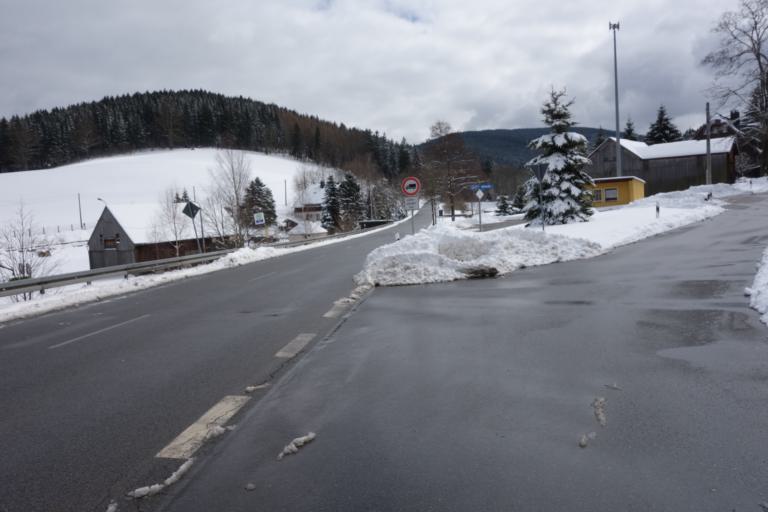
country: DE
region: Saxony
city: Rittersgrun
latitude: 50.4618
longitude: 12.8146
